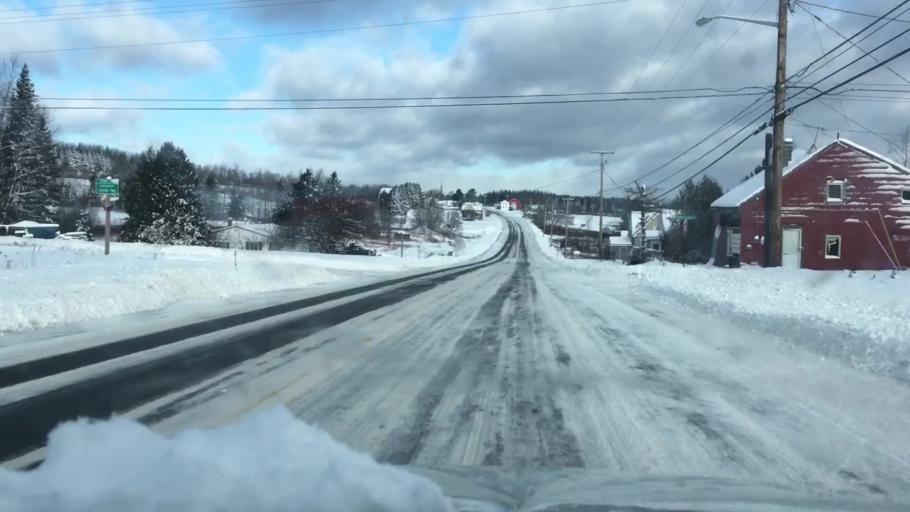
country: US
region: Maine
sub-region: Aroostook County
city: Caribou
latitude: 46.9560
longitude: -68.0279
